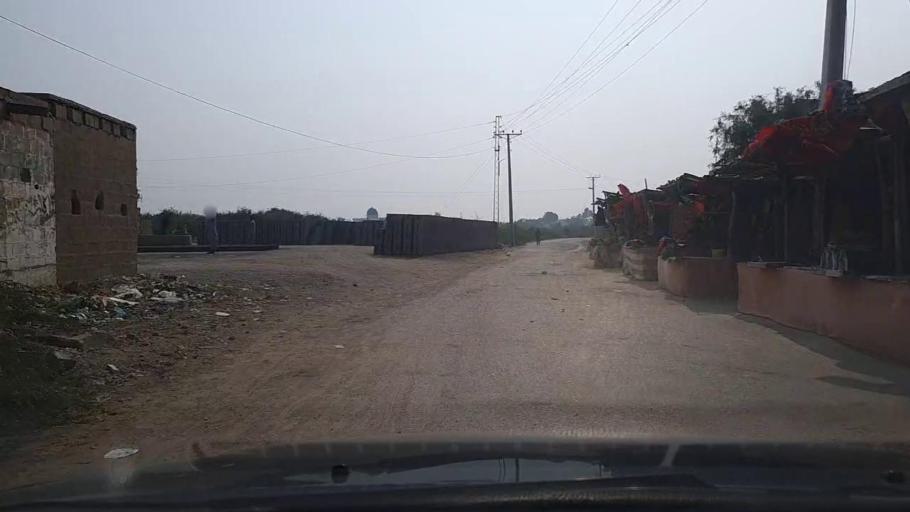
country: PK
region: Sindh
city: Thatta
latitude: 24.7498
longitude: 67.8980
